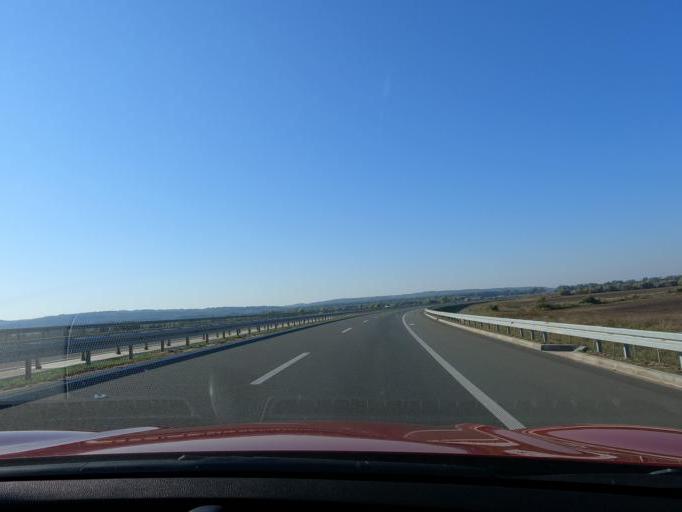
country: RS
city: Baric
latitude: 44.6878
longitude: 20.2675
